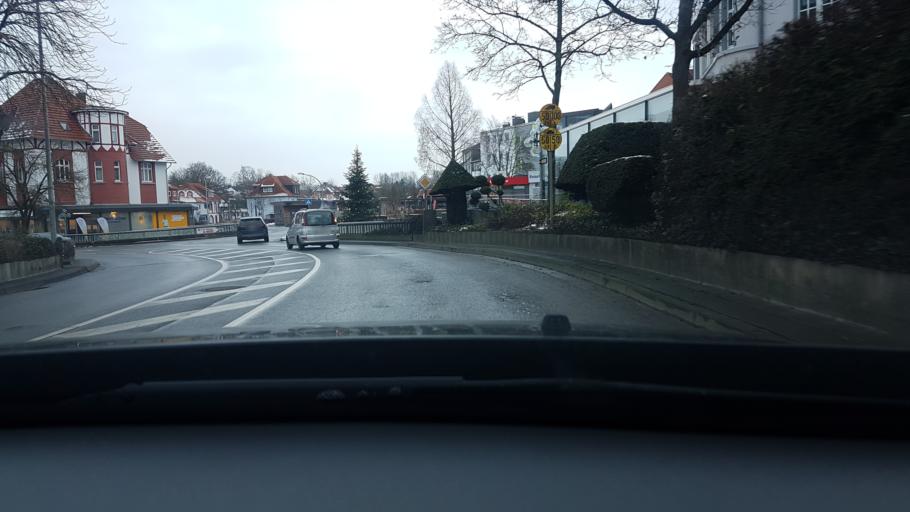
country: DE
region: Hesse
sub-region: Regierungsbezirk Kassel
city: Korbach
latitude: 51.2760
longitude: 8.8708
